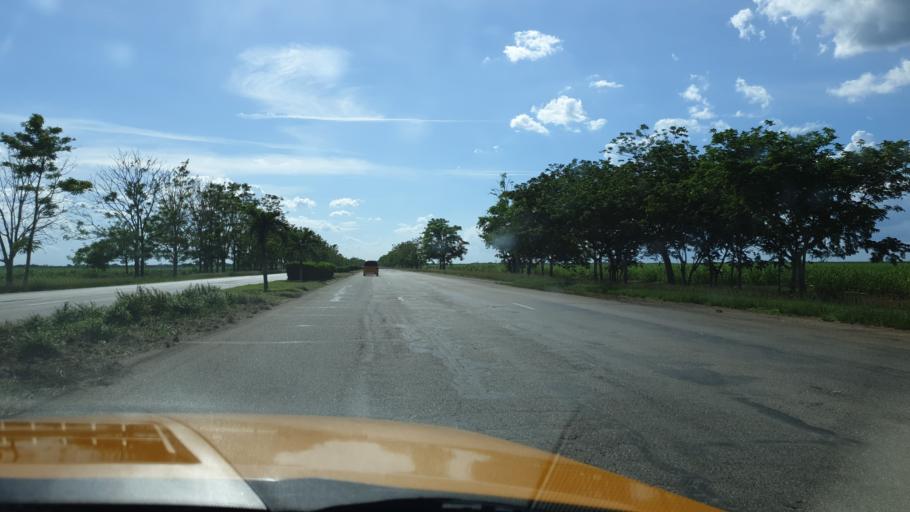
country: CU
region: Cienfuegos
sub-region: Municipio de Aguada de Pasajeros
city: Aguada de Pasajeros
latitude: 22.4125
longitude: -80.8984
